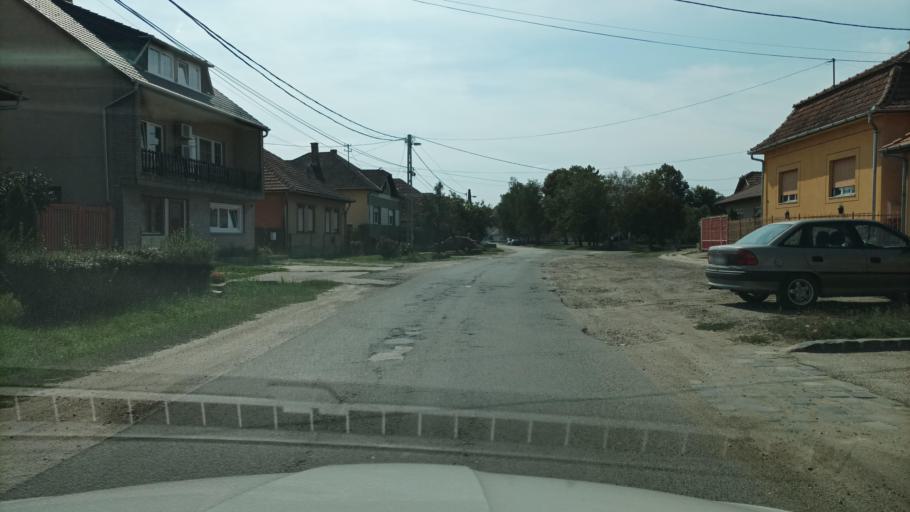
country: HU
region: Pest
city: Hevizgyoerk
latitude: 47.6331
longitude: 19.5210
